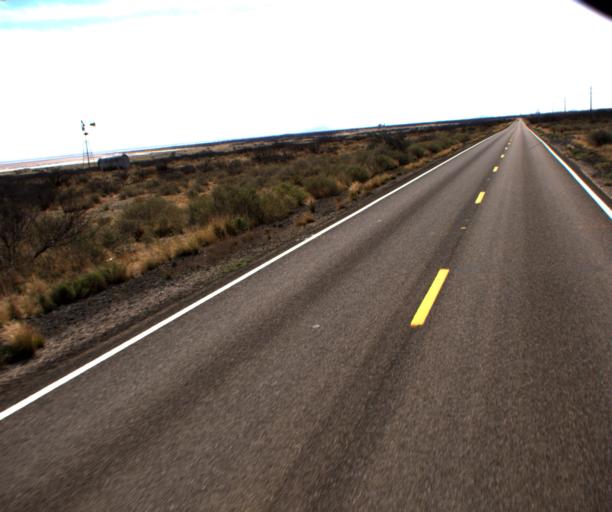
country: US
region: Arizona
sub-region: Cochise County
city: Willcox
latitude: 32.1598
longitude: -109.9410
